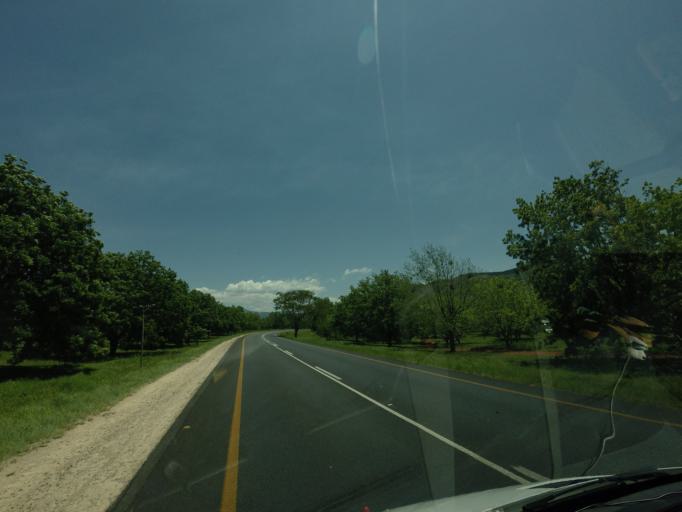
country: ZA
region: Mpumalanga
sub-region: Ehlanzeni District
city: Nelspruit
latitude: -25.4413
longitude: 30.6524
